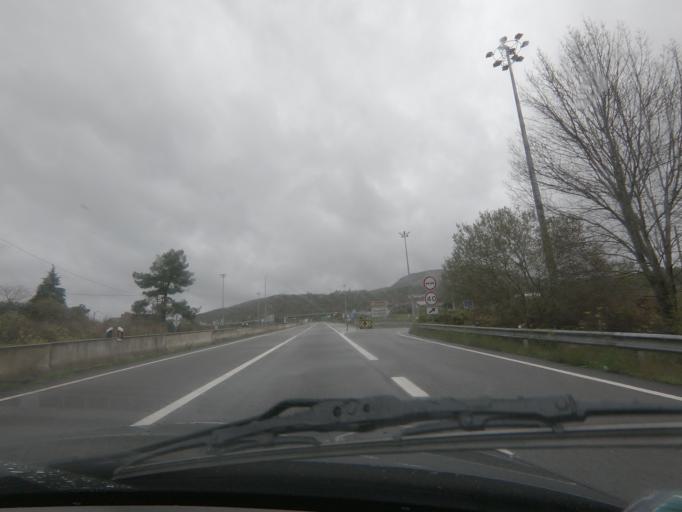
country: PT
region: Vila Real
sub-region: Vila Real
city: Vila Real
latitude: 41.2833
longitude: -7.8038
